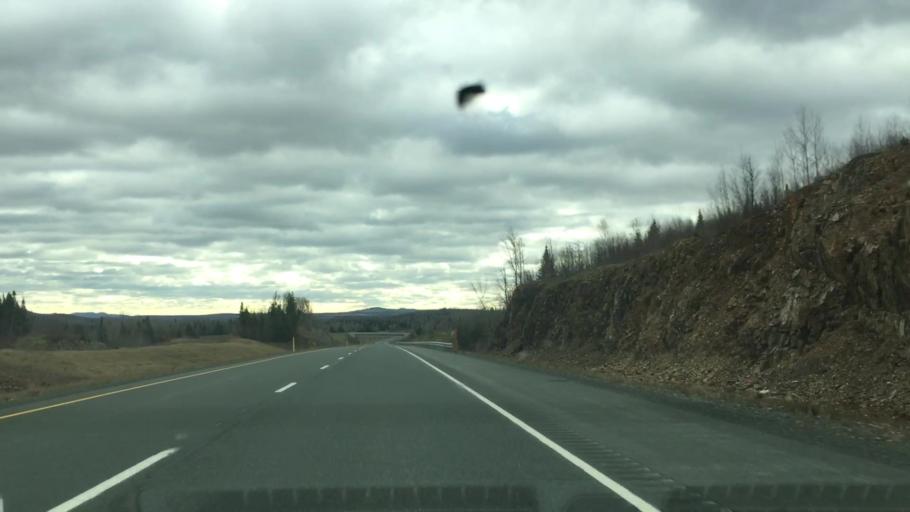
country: US
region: Maine
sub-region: Aroostook County
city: Easton
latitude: 46.6318
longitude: -67.7423
